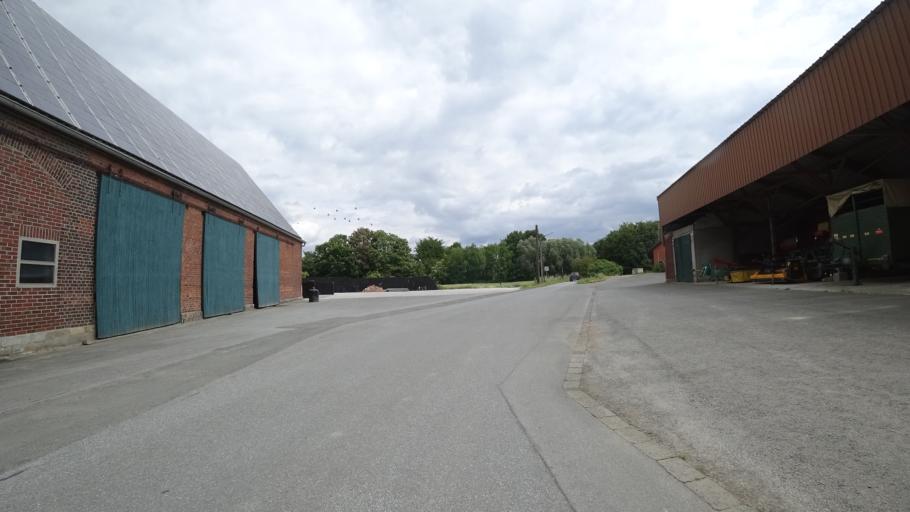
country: DE
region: North Rhine-Westphalia
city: Erwitte
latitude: 51.6278
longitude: 8.3714
